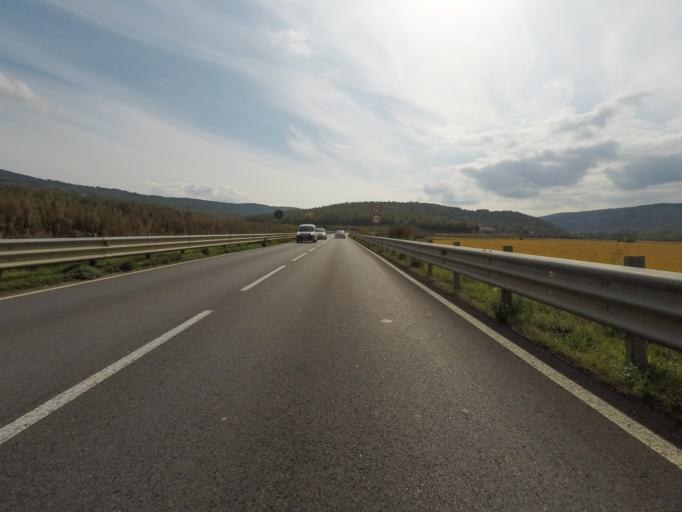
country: IT
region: Tuscany
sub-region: Provincia di Siena
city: Murlo
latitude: 43.1597
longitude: 11.2900
